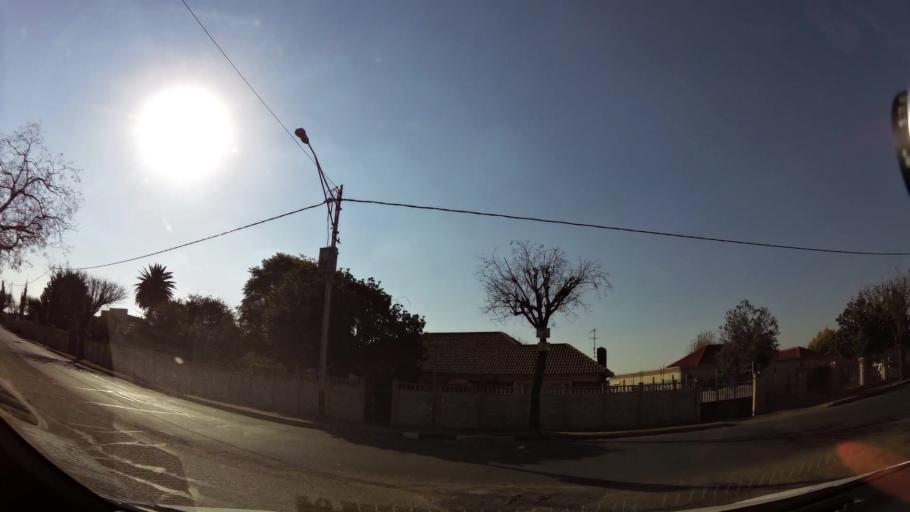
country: ZA
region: Gauteng
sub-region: City of Johannesburg Metropolitan Municipality
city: Johannesburg
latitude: -26.2453
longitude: 28.0119
